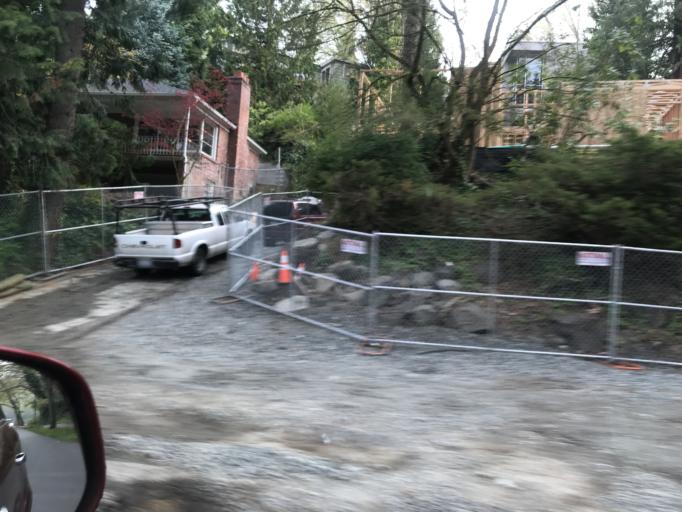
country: US
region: Washington
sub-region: King County
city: Seattle
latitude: 47.6237
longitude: -122.2874
